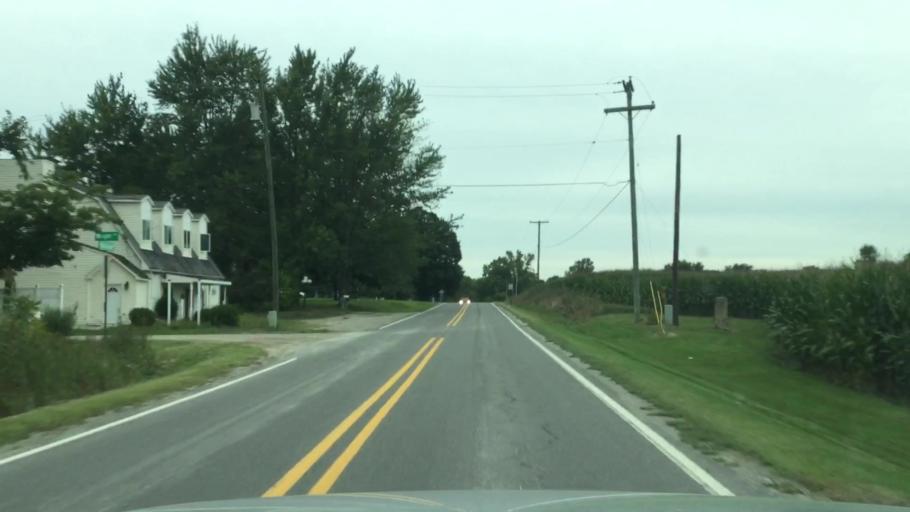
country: US
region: Michigan
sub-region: Washtenaw County
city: Milan
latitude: 42.1501
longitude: -83.6534
